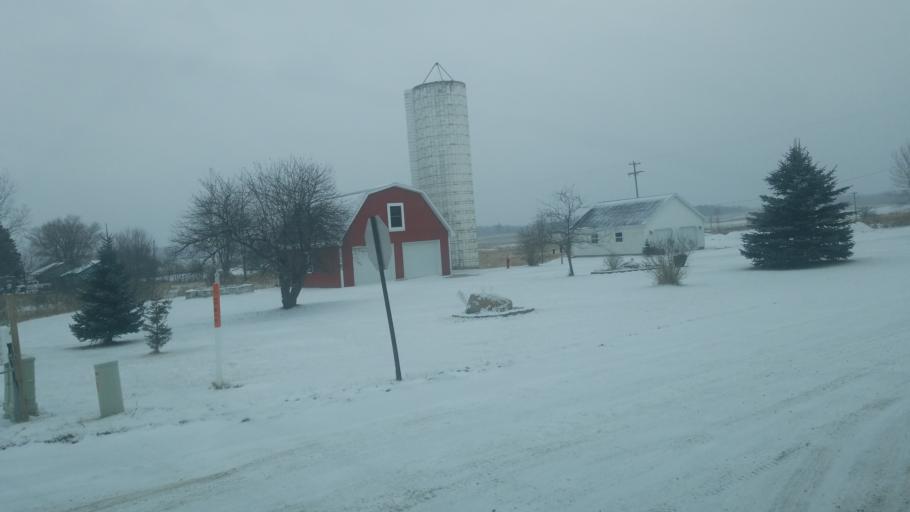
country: US
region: Michigan
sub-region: Osceola County
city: Evart
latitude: 44.1024
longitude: -85.1275
